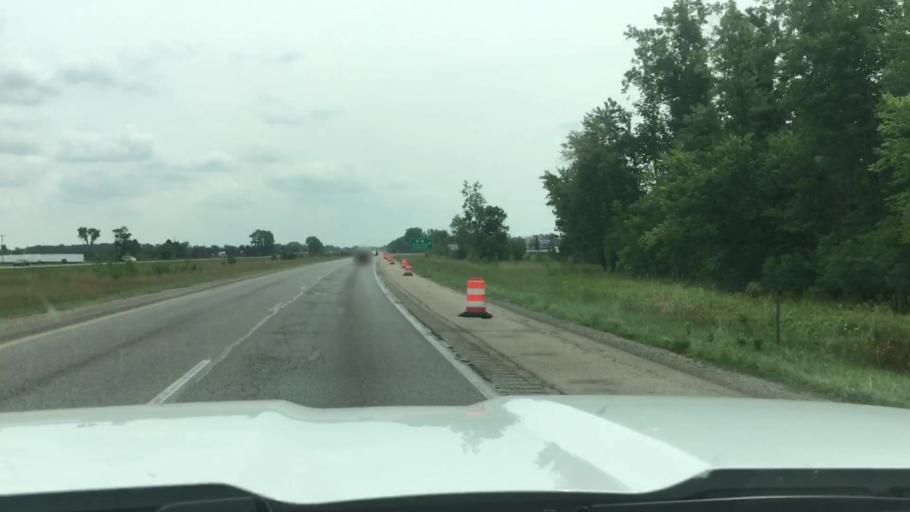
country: US
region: Michigan
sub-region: Ingham County
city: Webberville
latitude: 42.6636
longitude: -84.2080
